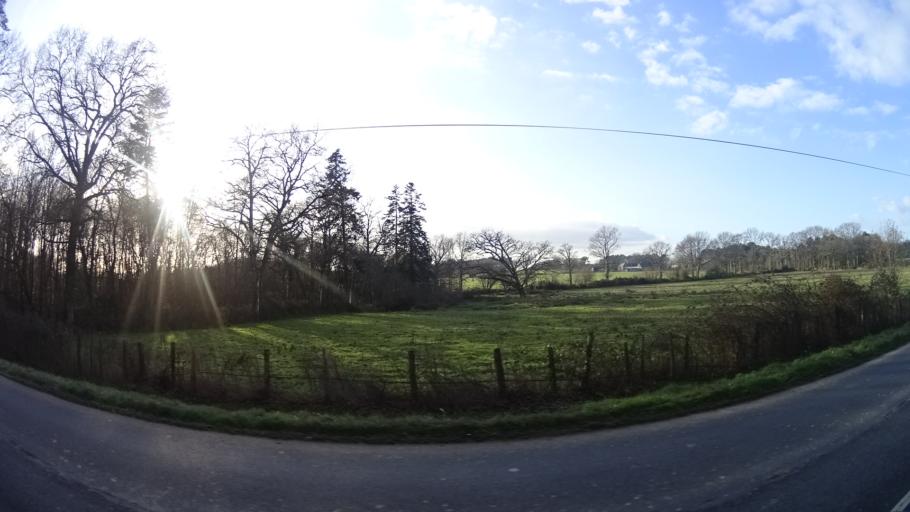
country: FR
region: Pays de la Loire
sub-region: Departement de la Loire-Atlantique
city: Saint-Nicolas-de-Redon
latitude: 47.6193
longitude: -2.0419
